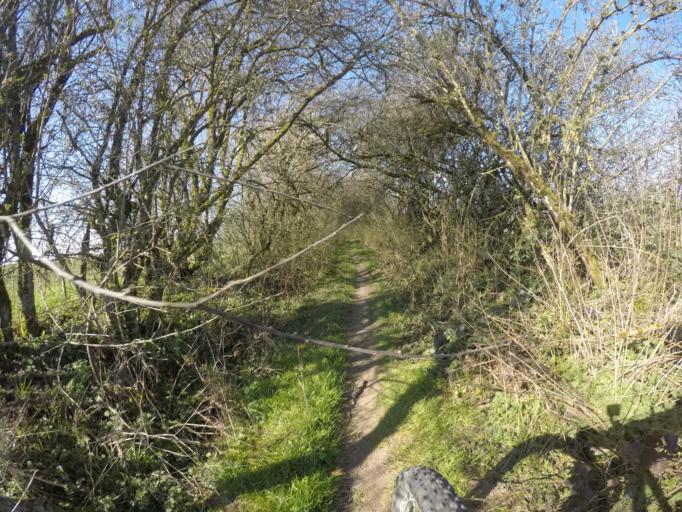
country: BE
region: Wallonia
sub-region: Province du Luxembourg
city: Tintigny
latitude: 49.7062
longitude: 5.5540
